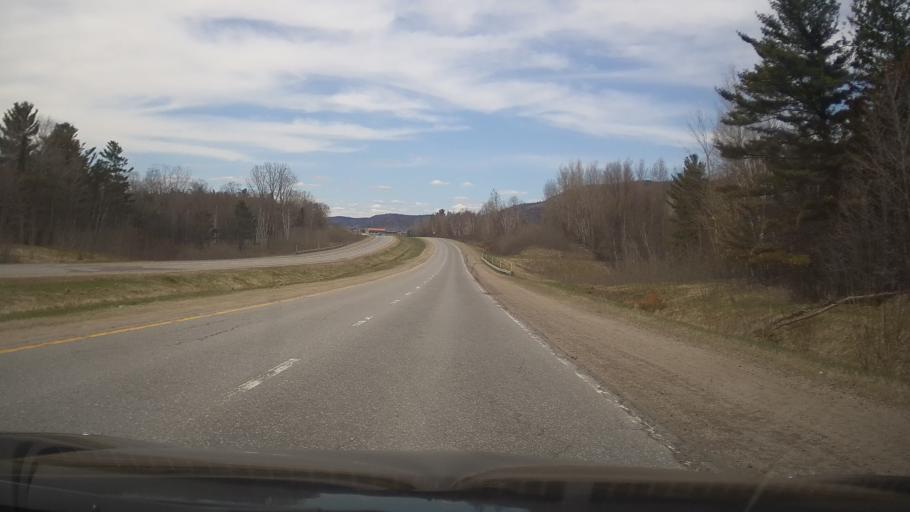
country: CA
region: Quebec
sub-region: Outaouais
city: Wakefield
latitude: 45.5304
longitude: -76.0048
